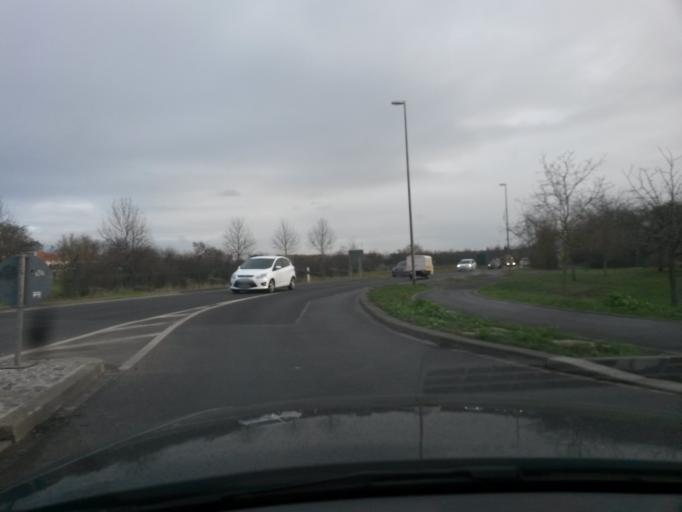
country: DE
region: Bavaria
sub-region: Regierungsbezirk Unterfranken
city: Gerbrunn
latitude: 49.7827
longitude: 9.9755
